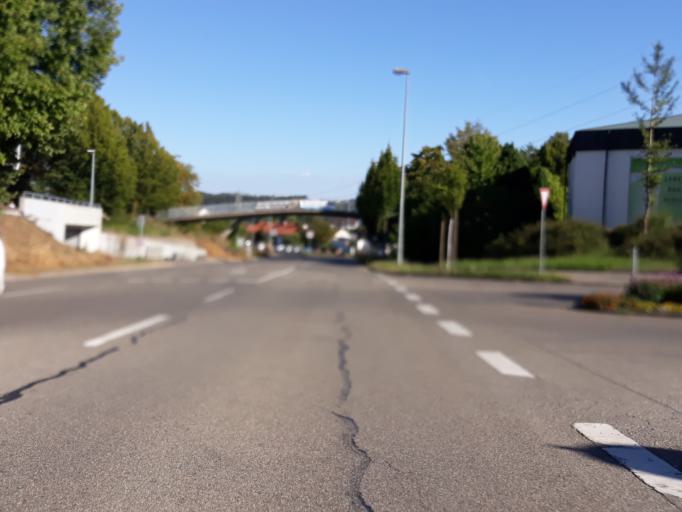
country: DE
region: Baden-Wuerttemberg
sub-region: Regierungsbezirk Stuttgart
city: Holzgerlingen
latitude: 48.6453
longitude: 9.0137
